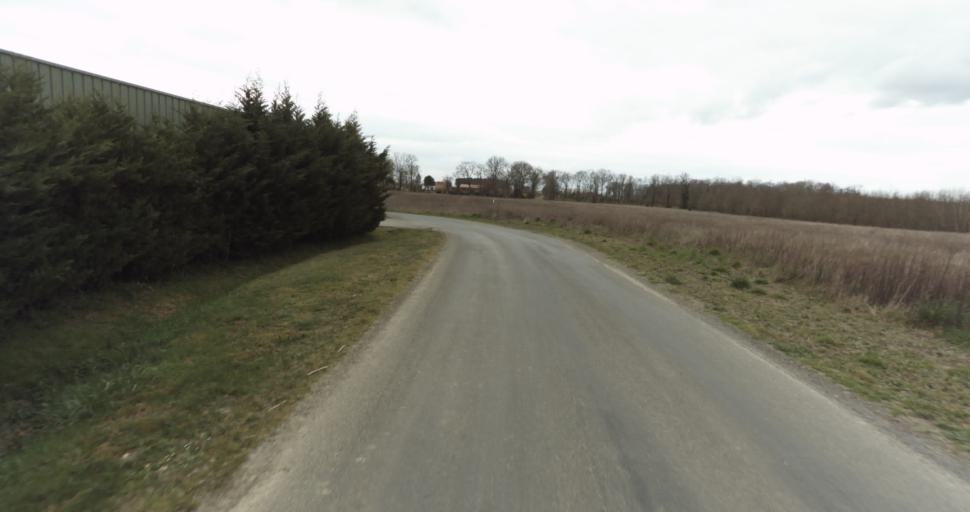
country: FR
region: Aquitaine
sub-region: Departement des Landes
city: Sarbazan
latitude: 44.0145
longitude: -0.3347
